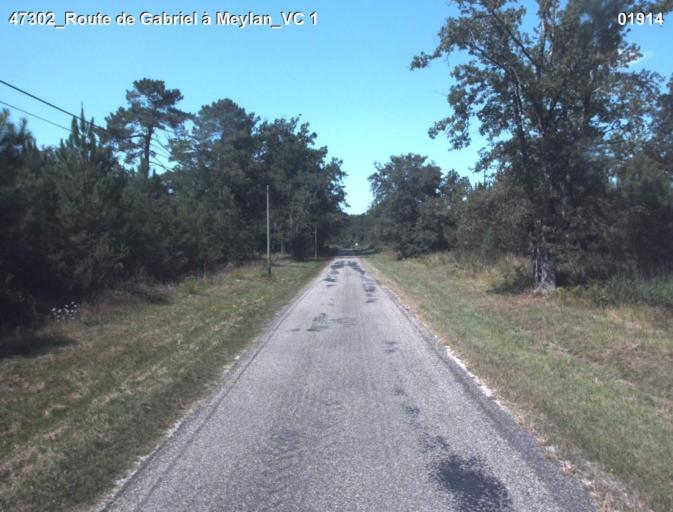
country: FR
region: Aquitaine
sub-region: Departement du Lot-et-Garonne
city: Mezin
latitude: 44.0676
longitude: 0.1381
